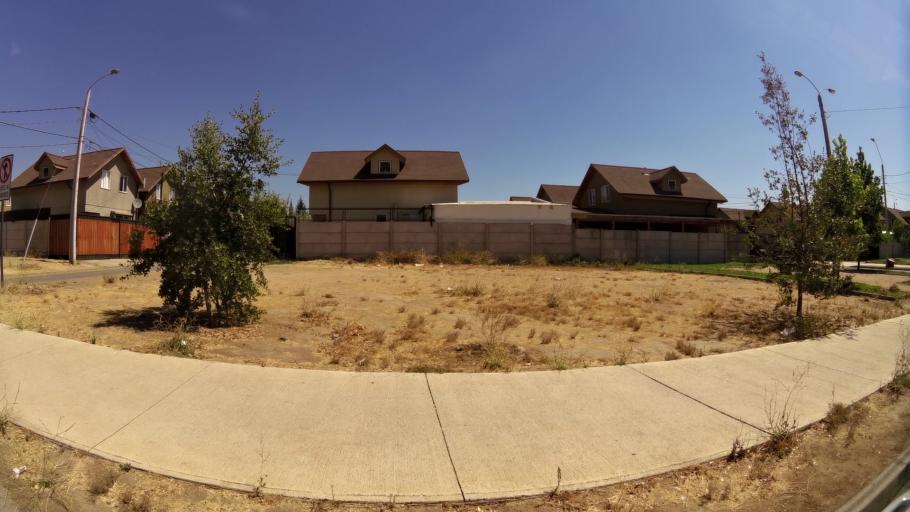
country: CL
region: Maule
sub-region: Provincia de Talca
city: Talca
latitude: -35.4037
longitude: -71.6428
